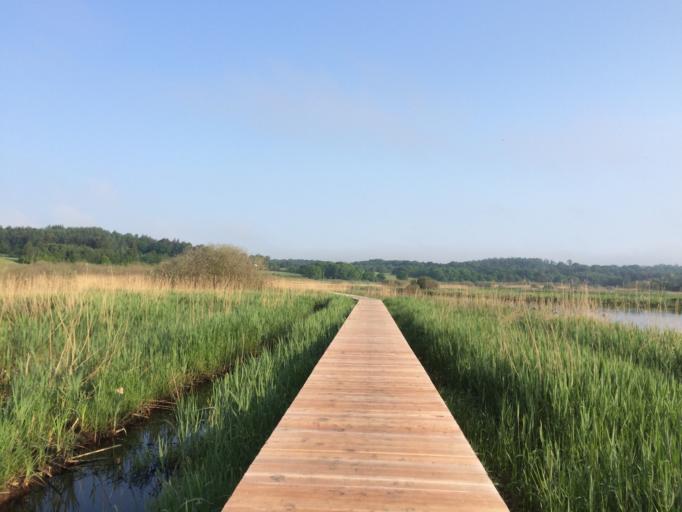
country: DK
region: Central Jutland
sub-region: Silkeborg Kommune
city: Svejbaek
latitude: 56.1956
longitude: 9.6525
